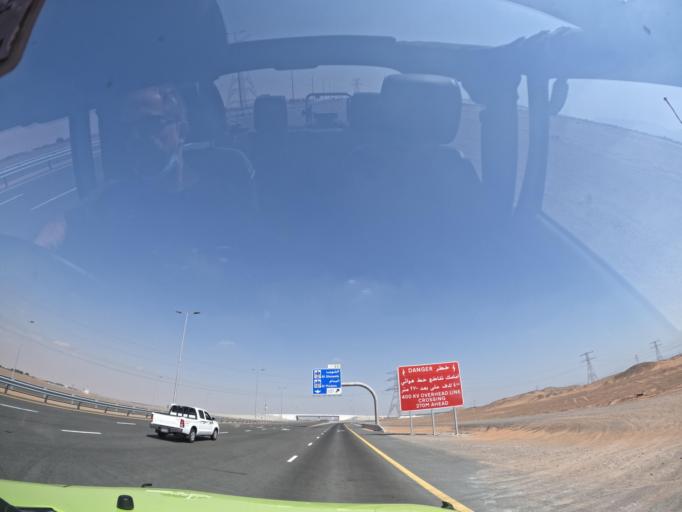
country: AE
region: Ash Shariqah
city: Adh Dhayd
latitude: 24.8093
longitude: 55.8017
